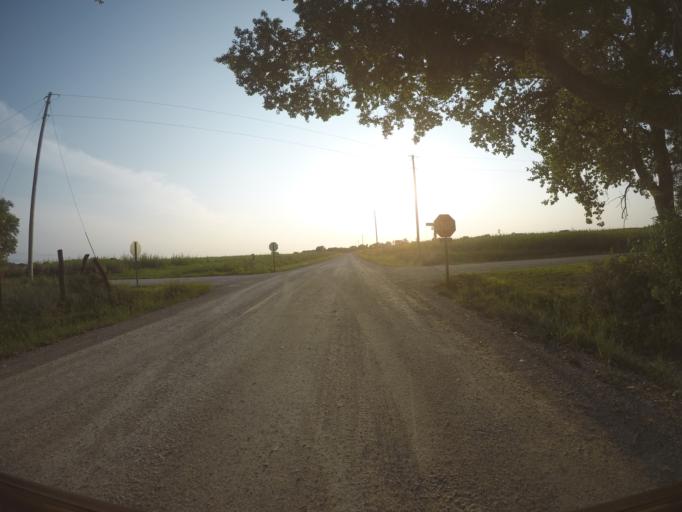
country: US
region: Kansas
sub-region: Riley County
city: Manhattan
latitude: 39.1304
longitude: -96.4637
